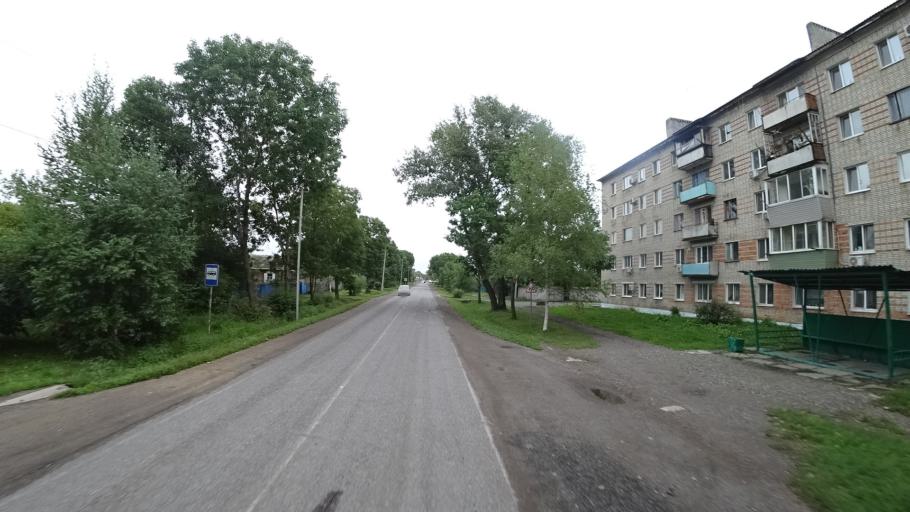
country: RU
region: Primorskiy
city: Chernigovka
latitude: 44.3460
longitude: 132.5703
